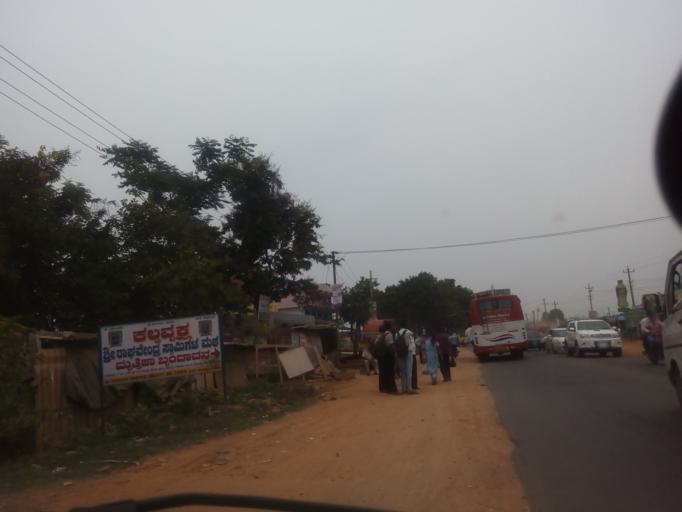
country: IN
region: Karnataka
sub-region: Bangalore Rural
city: Nelamangala
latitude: 12.9908
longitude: 77.4544
